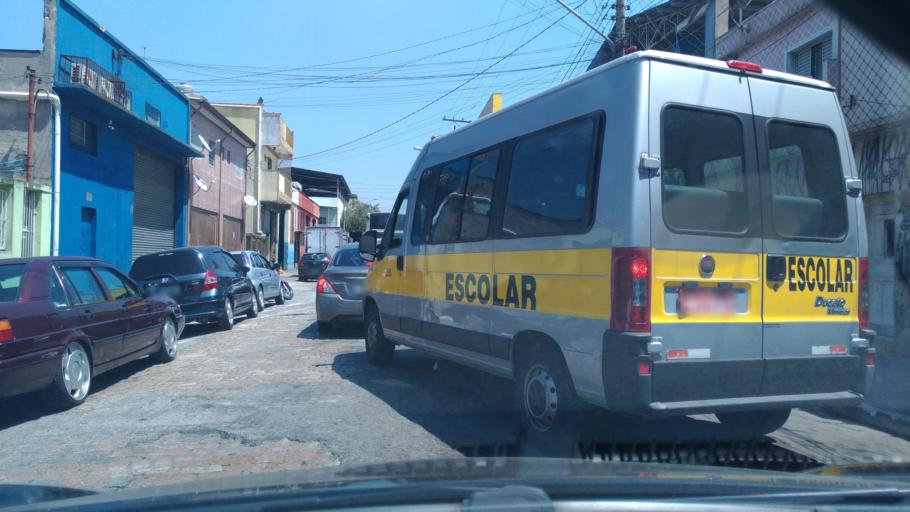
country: BR
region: Sao Paulo
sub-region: Sao Paulo
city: Sao Paulo
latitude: -23.5191
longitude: -46.5798
